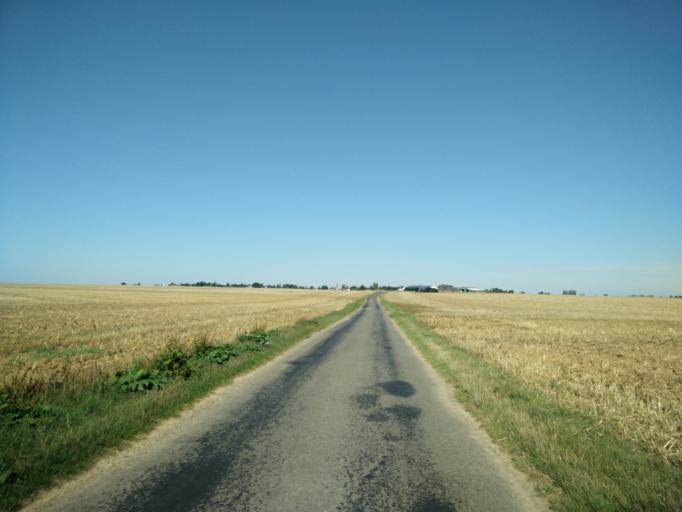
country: FR
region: Haute-Normandie
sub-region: Departement de l'Eure
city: Saint-Pierre-des-Fleurs
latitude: 49.1734
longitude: 0.9991
